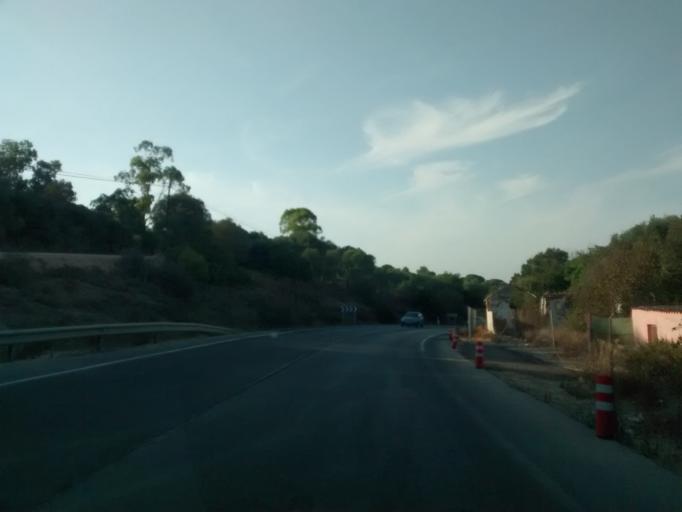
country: ES
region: Andalusia
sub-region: Provincia de Cadiz
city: Vejer de la Frontera
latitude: 36.2267
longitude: -5.9486
